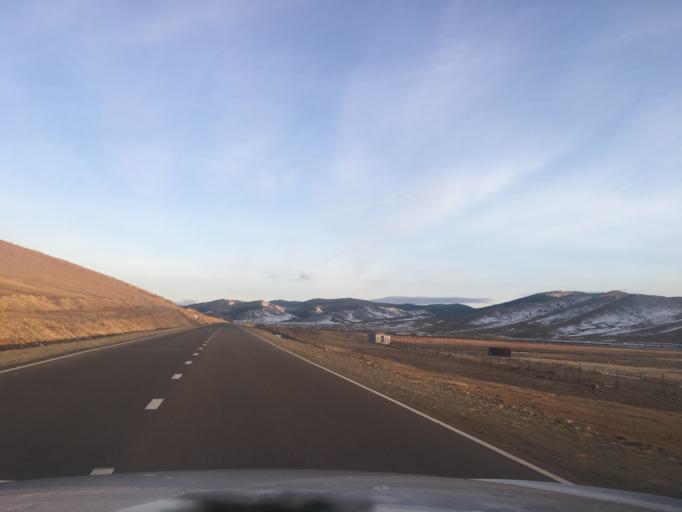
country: MN
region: Central Aimak
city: Mandal
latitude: 48.1133
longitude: 106.7044
